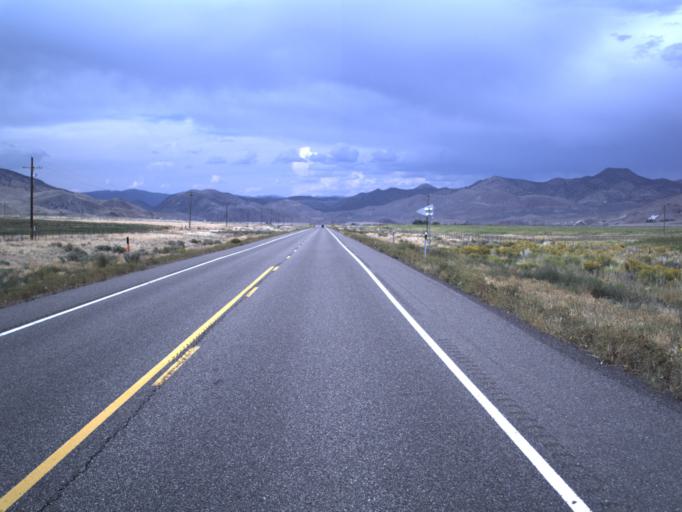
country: US
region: Utah
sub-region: Piute County
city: Junction
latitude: 38.4181
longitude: -112.2315
